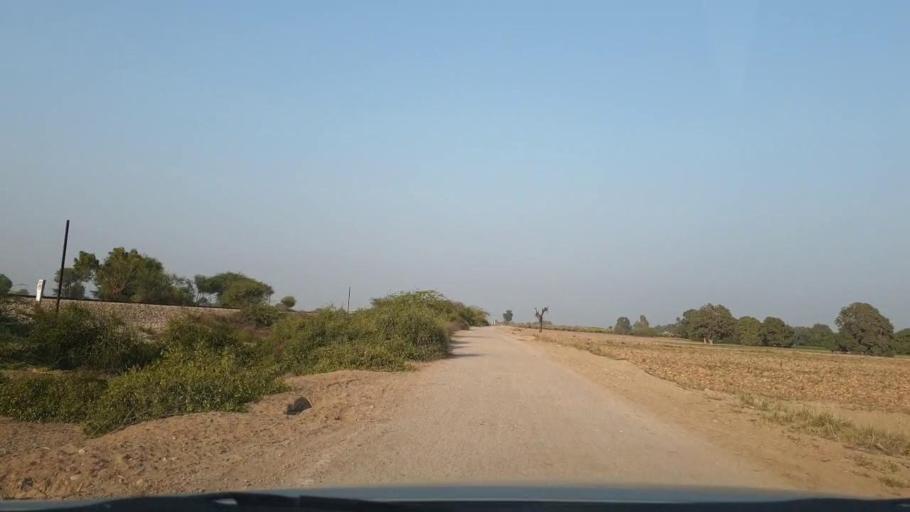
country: PK
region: Sindh
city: Tando Adam
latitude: 25.6967
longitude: 68.6367
